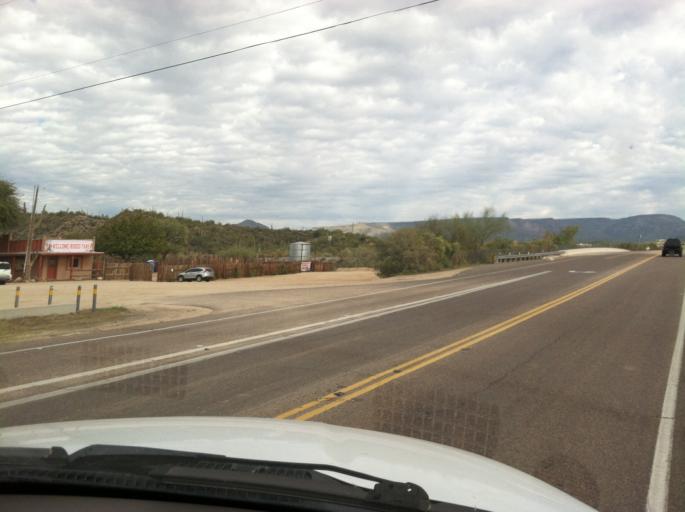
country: US
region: Arizona
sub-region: Maricopa County
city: New River
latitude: 33.9180
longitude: -112.1407
